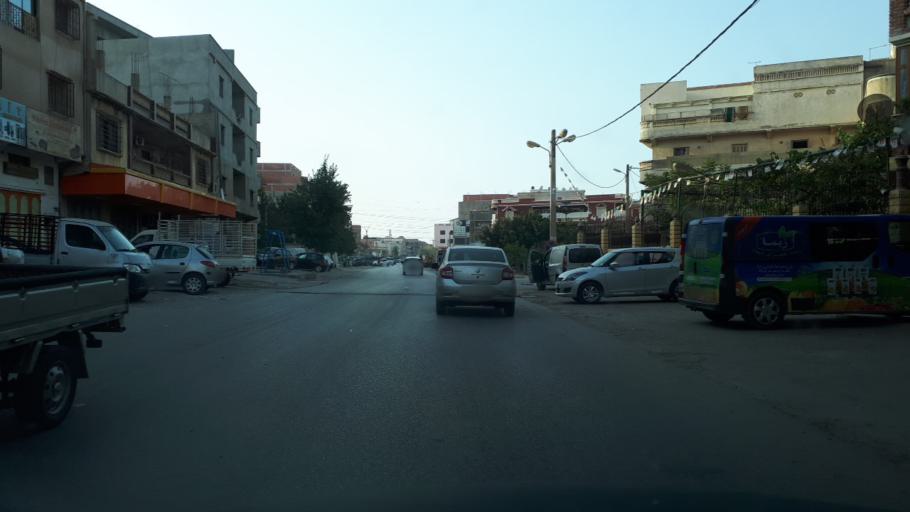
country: DZ
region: Alger
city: Dar el Beida
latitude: 36.7321
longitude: 3.2356
